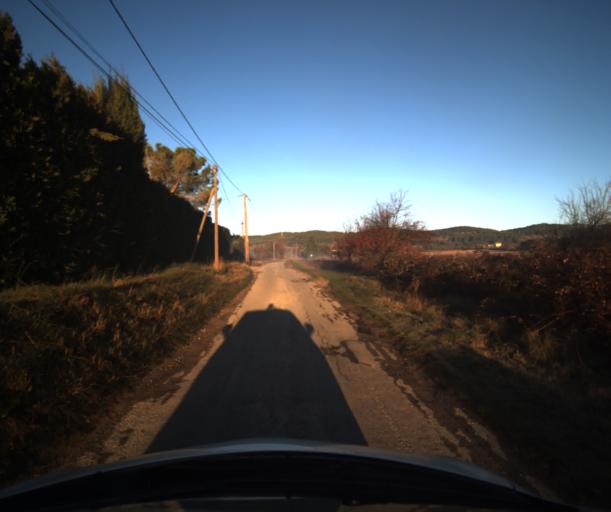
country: FR
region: Provence-Alpes-Cote d'Azur
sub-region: Departement du Vaucluse
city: Pertuis
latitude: 43.7021
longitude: 5.4917
